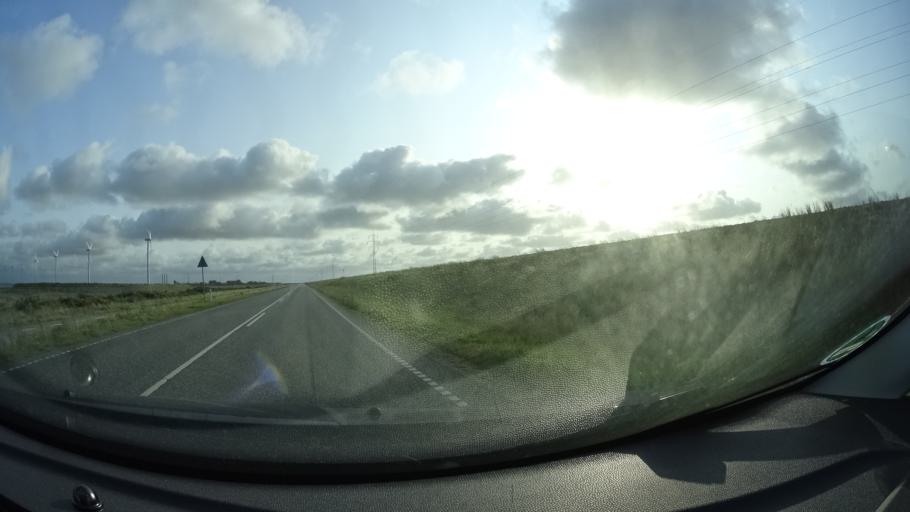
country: DK
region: Central Jutland
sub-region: Lemvig Kommune
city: Thyboron
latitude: 56.6769
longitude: 8.2202
